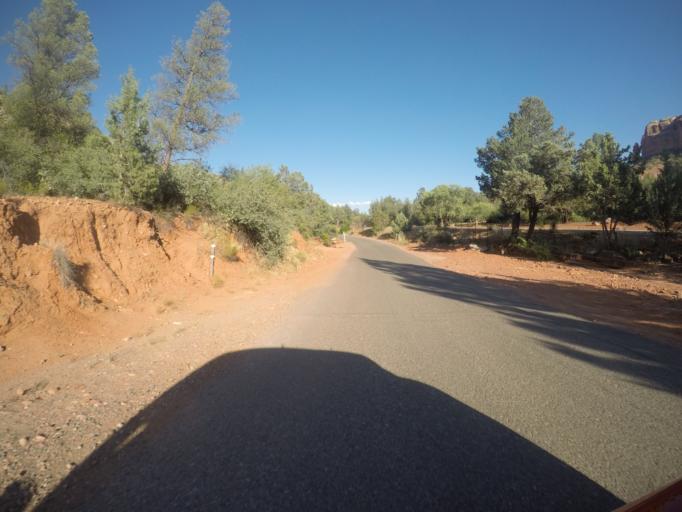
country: US
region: Arizona
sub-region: Yavapai County
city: West Sedona
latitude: 34.8278
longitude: -111.7926
